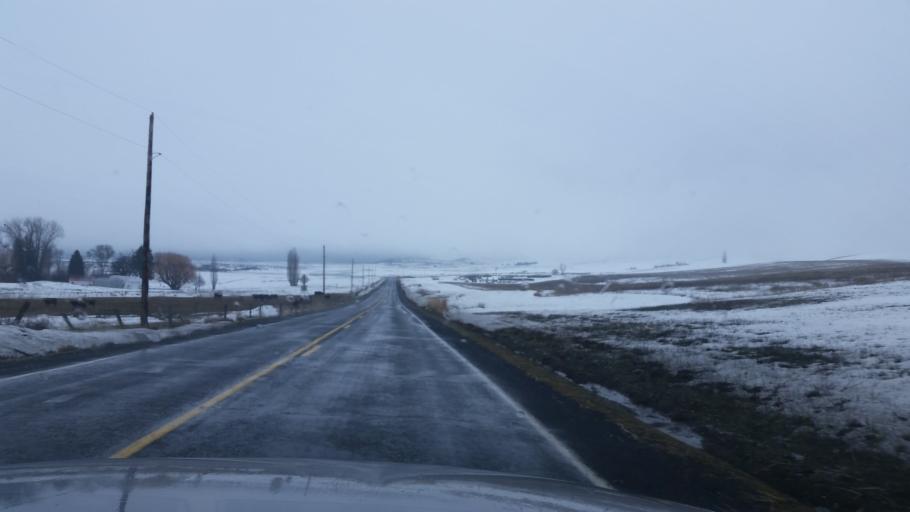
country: US
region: Washington
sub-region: Lincoln County
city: Davenport
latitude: 47.3414
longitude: -118.0047
